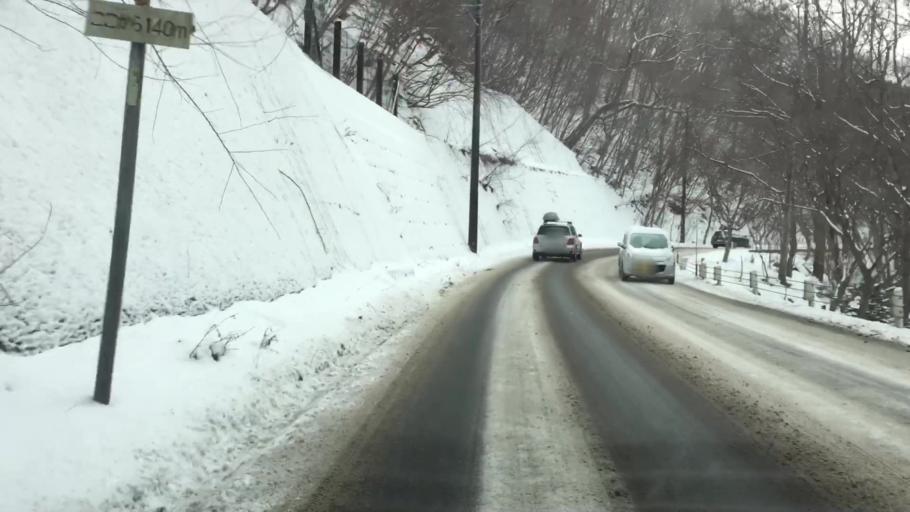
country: JP
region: Tochigi
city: Yaita
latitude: 36.9714
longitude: 139.7927
